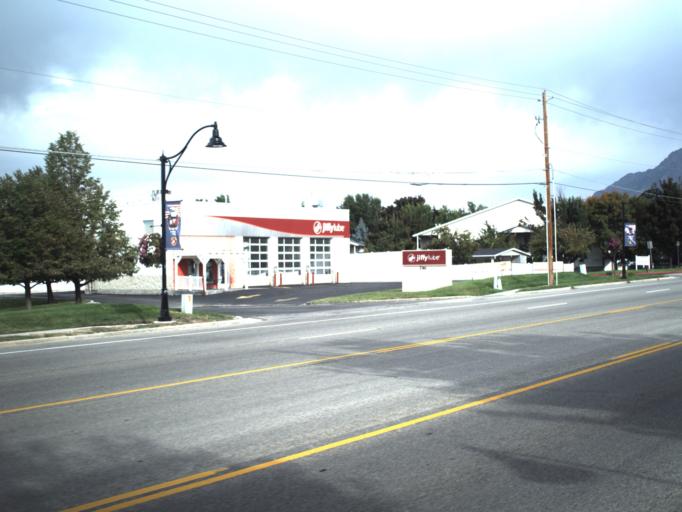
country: US
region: Utah
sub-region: Weber County
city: North Ogden
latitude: 41.3015
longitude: -111.9687
